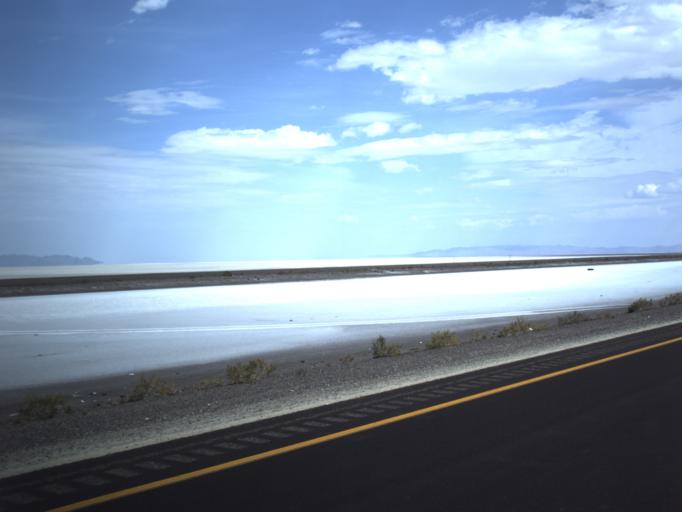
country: US
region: Utah
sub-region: Tooele County
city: Wendover
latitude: 40.7341
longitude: -113.6427
